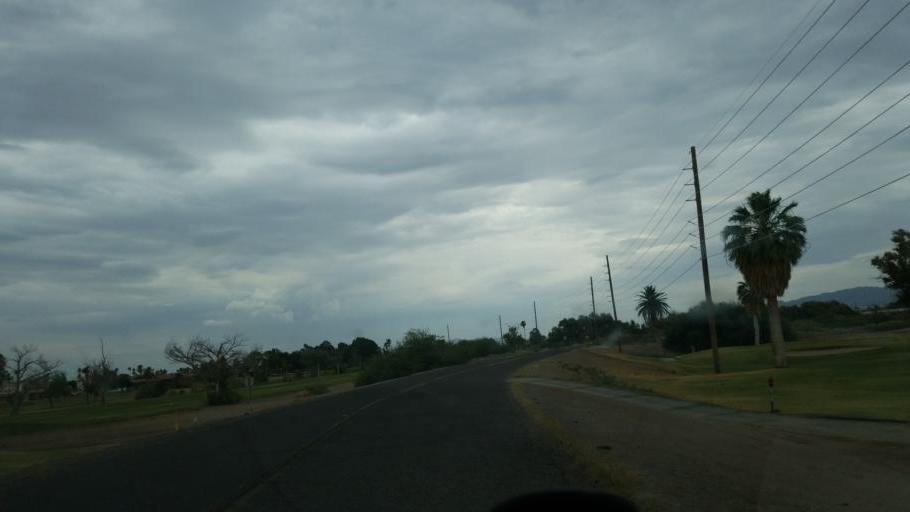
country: US
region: California
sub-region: San Bernardino County
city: Needles
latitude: 34.8432
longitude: -114.6011
